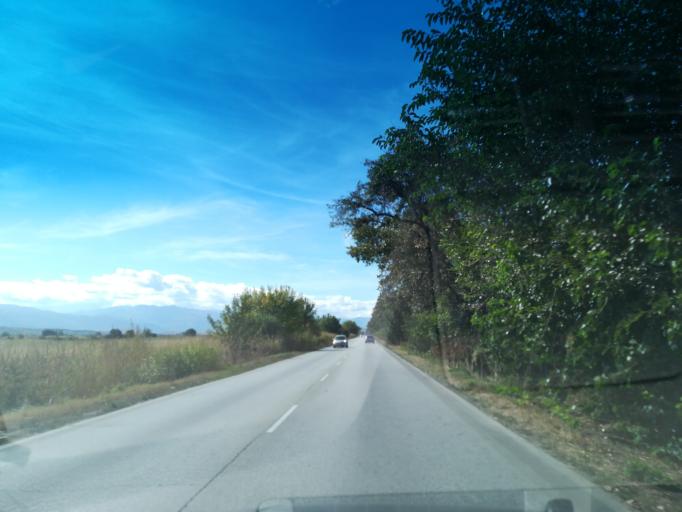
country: BG
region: Plovdiv
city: Stamboliyski
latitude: 42.1260
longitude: 24.5899
